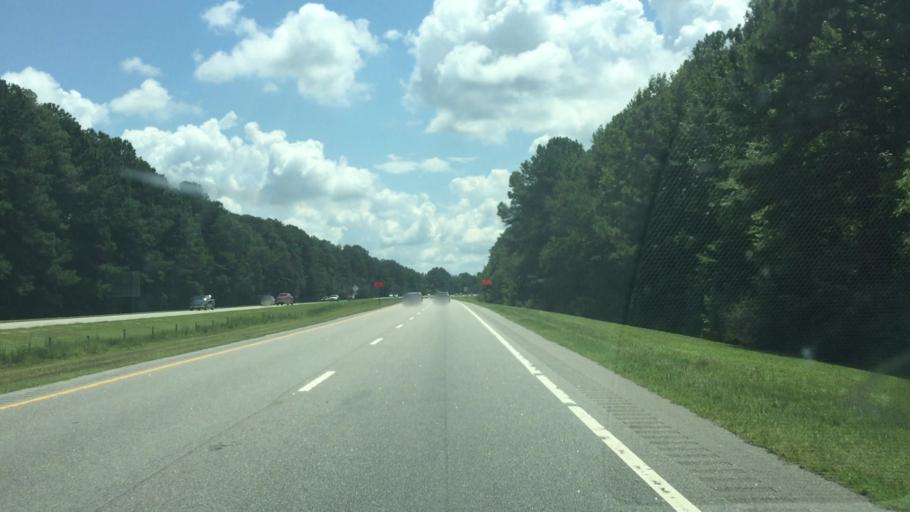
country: US
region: North Carolina
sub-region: Robeson County
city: Lumberton
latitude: 34.5752
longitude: -79.0403
